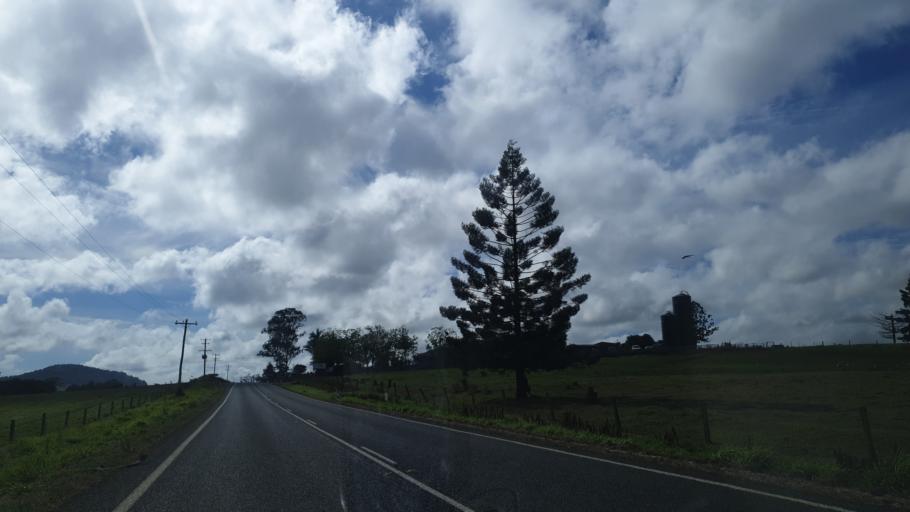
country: AU
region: Queensland
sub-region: Tablelands
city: Atherton
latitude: -17.2959
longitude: 145.5380
